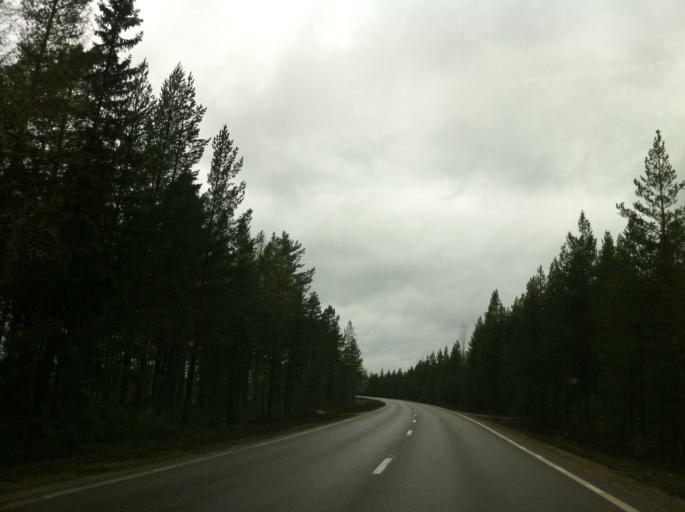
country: SE
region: Jaemtland
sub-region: Harjedalens Kommun
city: Sveg
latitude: 62.1358
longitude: 14.0449
